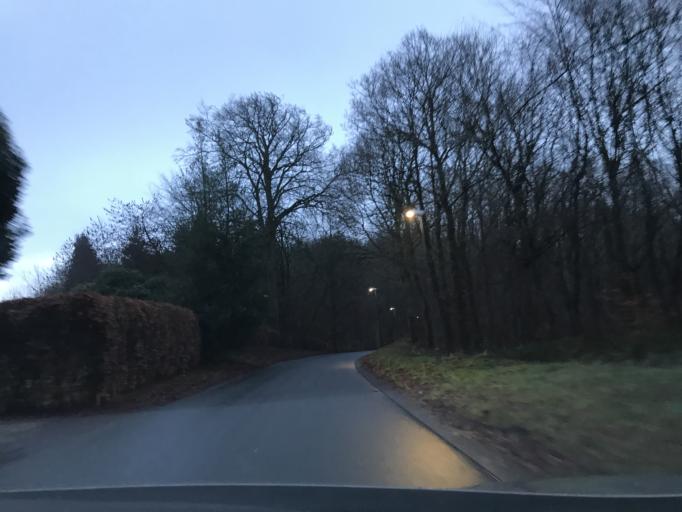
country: DK
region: South Denmark
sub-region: Vejle Kommune
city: Brejning
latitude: 55.6866
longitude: 9.7650
